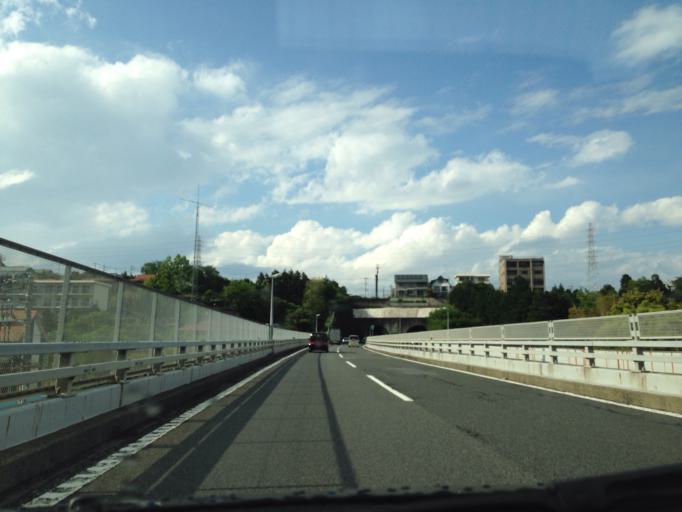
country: JP
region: Kanagawa
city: Odawara
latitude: 35.2726
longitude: 139.1503
